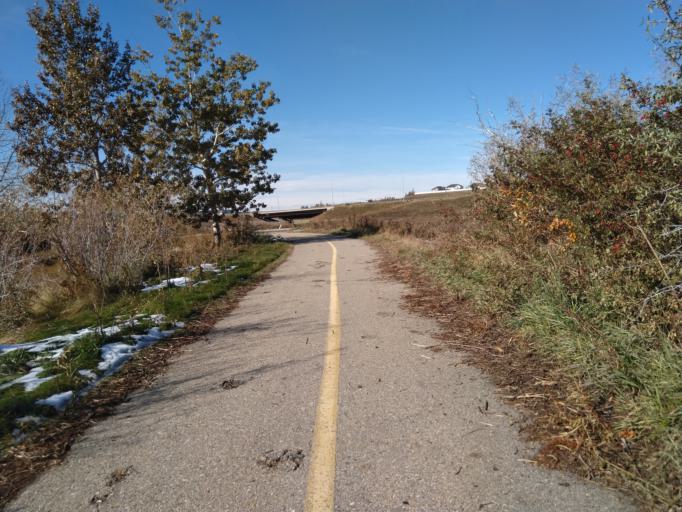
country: CA
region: Alberta
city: Calgary
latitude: 51.1570
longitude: -114.1083
